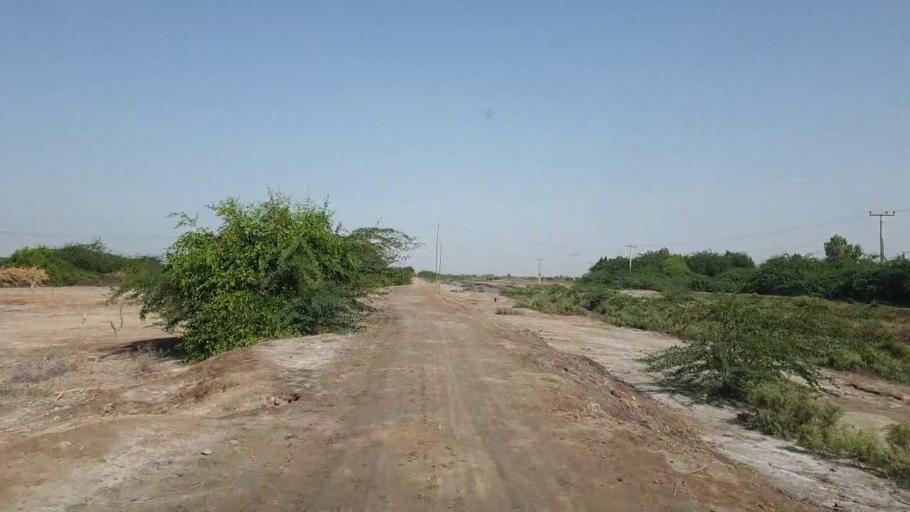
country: PK
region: Sindh
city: Tando Bago
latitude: 24.6994
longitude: 69.0705
